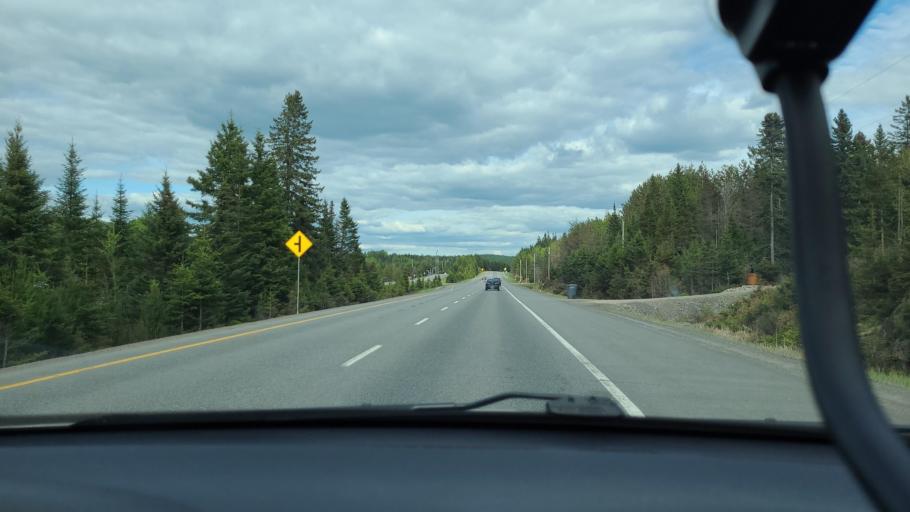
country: CA
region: Quebec
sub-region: Laurentides
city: Sainte-Agathe-des-Monts
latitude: 46.1033
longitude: -74.4090
